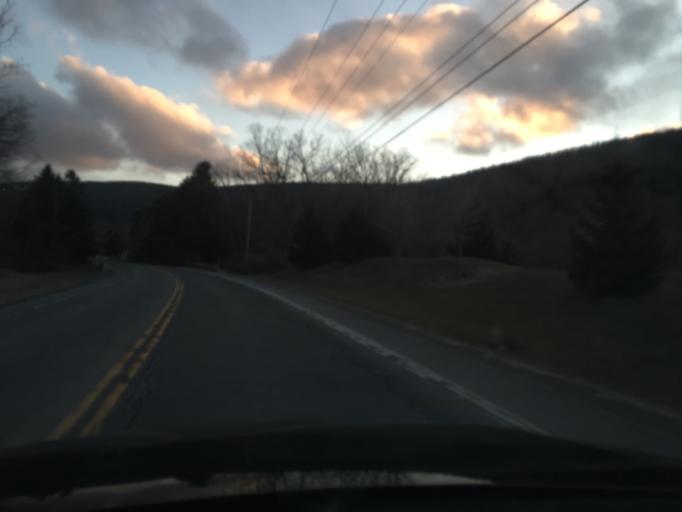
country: US
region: New York
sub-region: Ontario County
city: Holcomb
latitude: 42.7767
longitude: -77.4033
